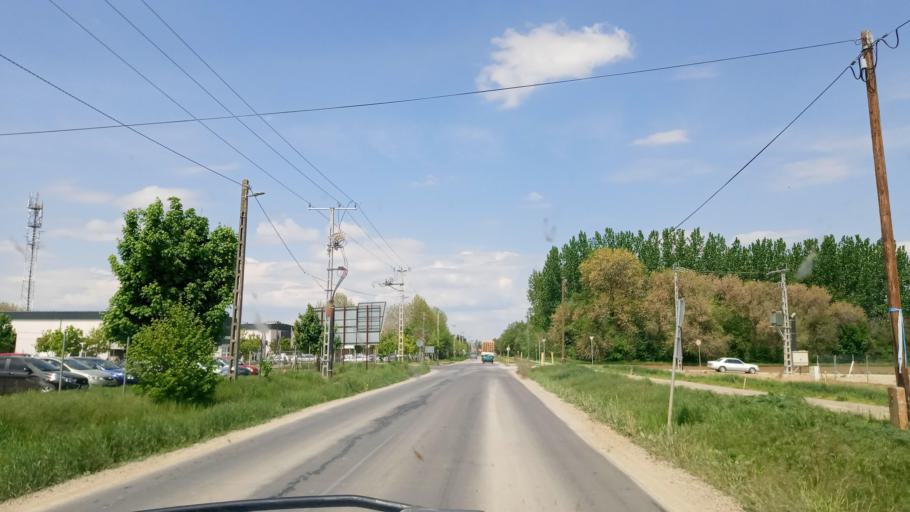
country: HU
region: Baranya
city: Boly
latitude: 45.9559
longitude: 18.5287
